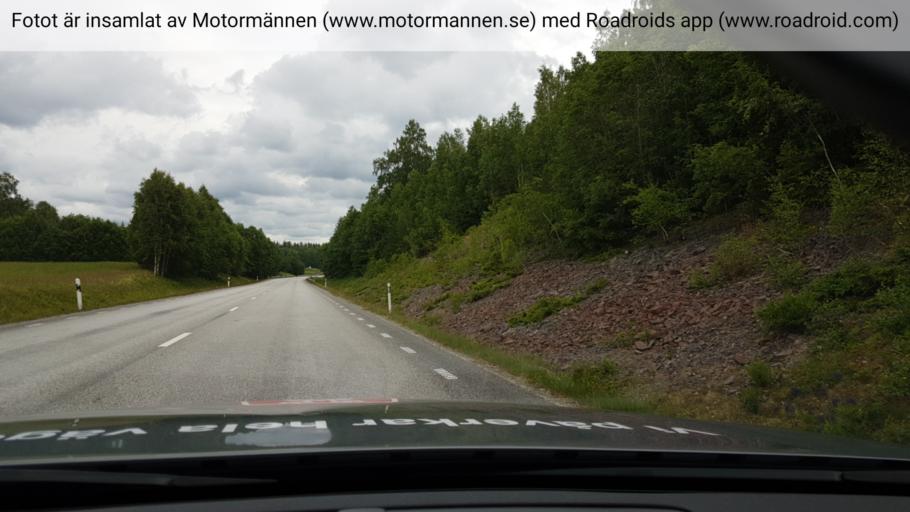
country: SE
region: OErebro
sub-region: Lindesbergs Kommun
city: Lindesberg
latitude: 59.6419
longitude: 15.2302
